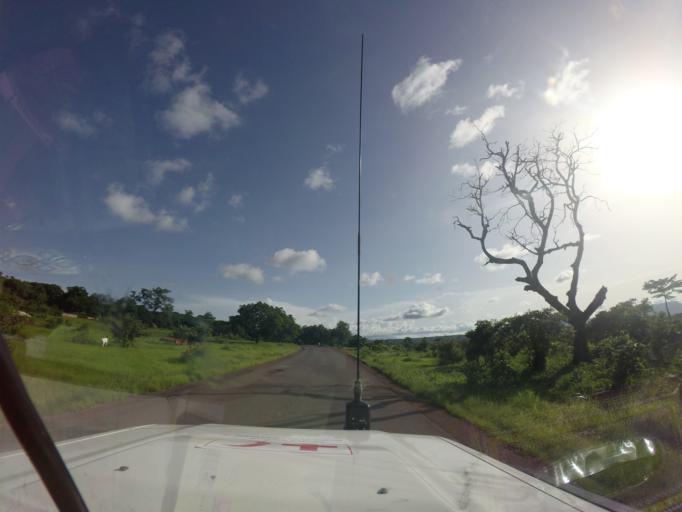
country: GN
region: Kindia
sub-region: Kindia
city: Kindia
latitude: 10.0766
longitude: -12.6484
